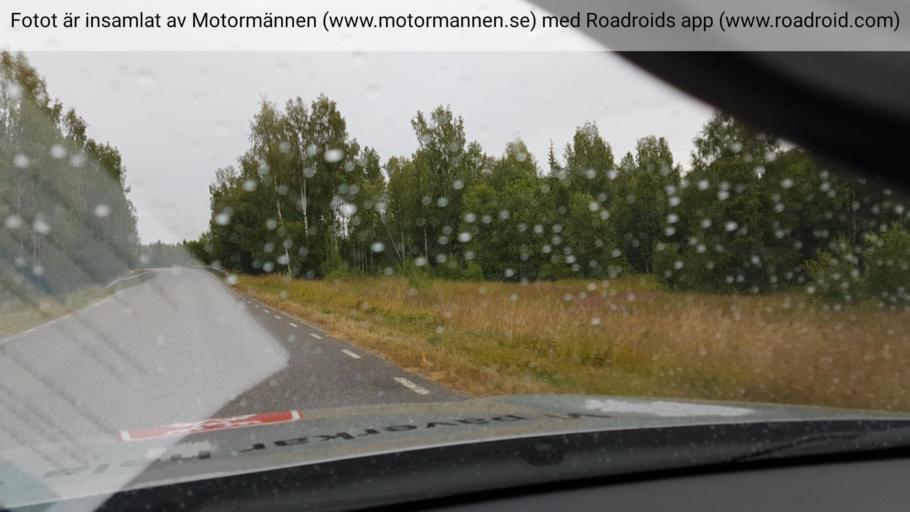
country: SE
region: Norrbotten
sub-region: Bodens Kommun
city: Boden
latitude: 65.8727
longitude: 21.3805
